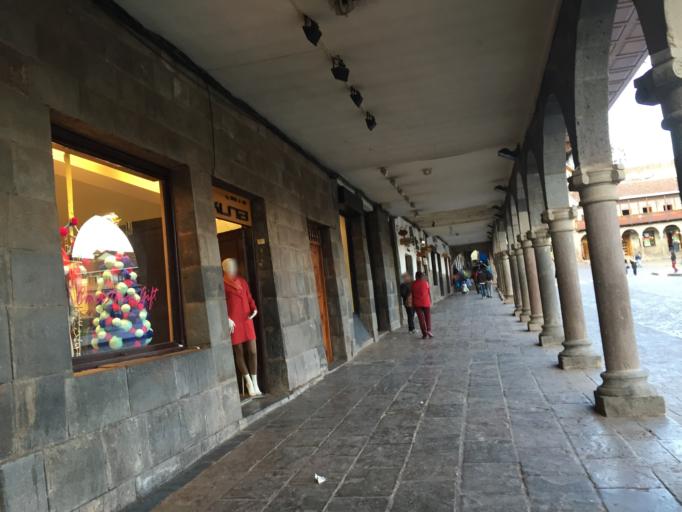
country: PE
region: Cusco
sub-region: Provincia de Cusco
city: Cusco
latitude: -13.5163
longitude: -71.9794
